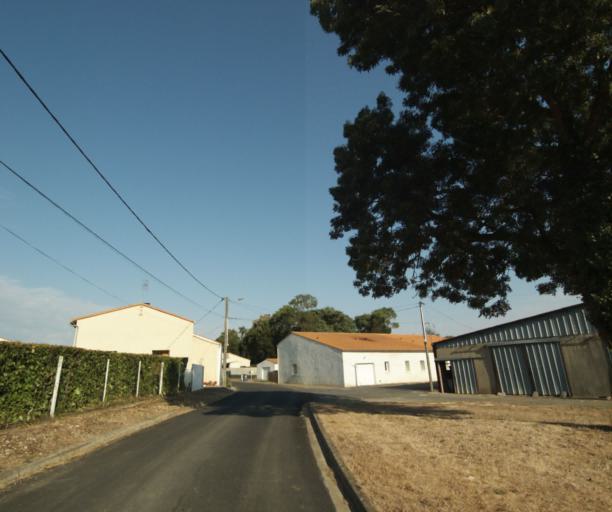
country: FR
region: Poitou-Charentes
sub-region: Departement de la Charente-Maritime
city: Muron
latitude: 45.9835
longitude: -0.8197
